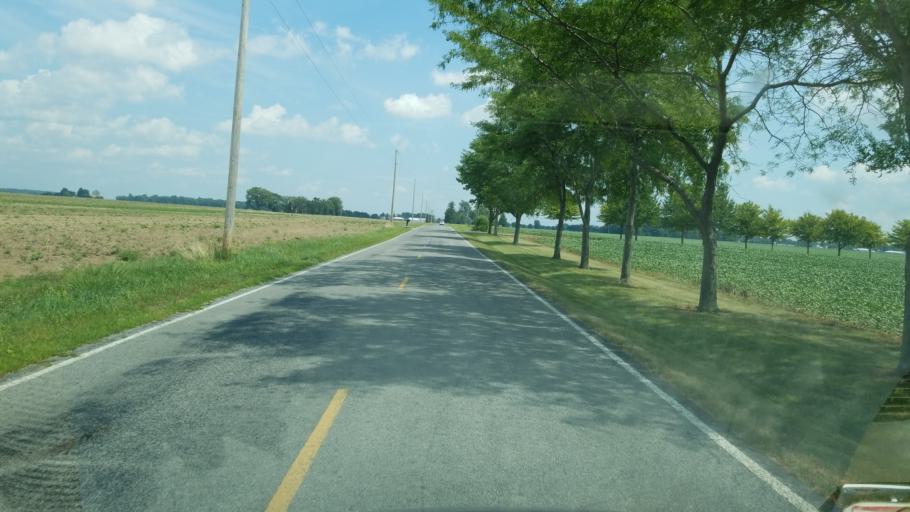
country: US
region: Ohio
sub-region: Hancock County
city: Arlington
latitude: 40.9068
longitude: -83.6689
